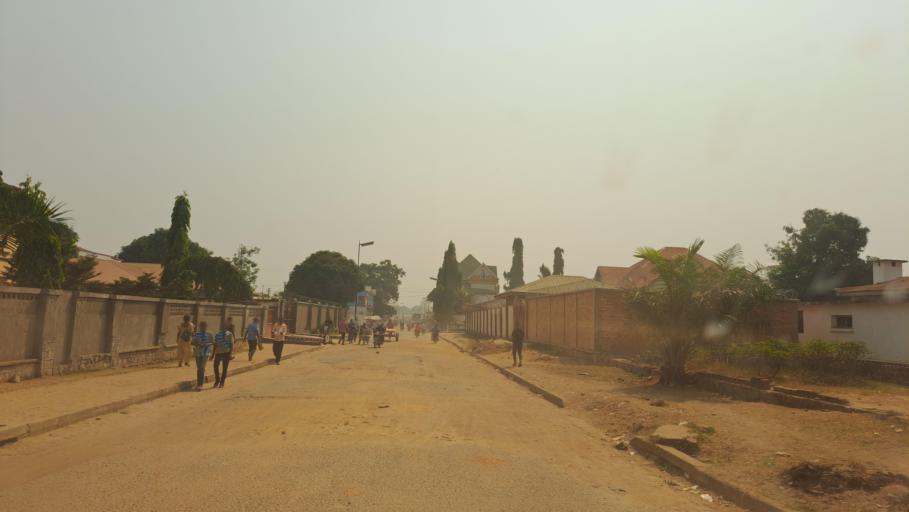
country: CD
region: Kasai-Occidental
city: Kananga
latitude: -5.8986
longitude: 22.4068
